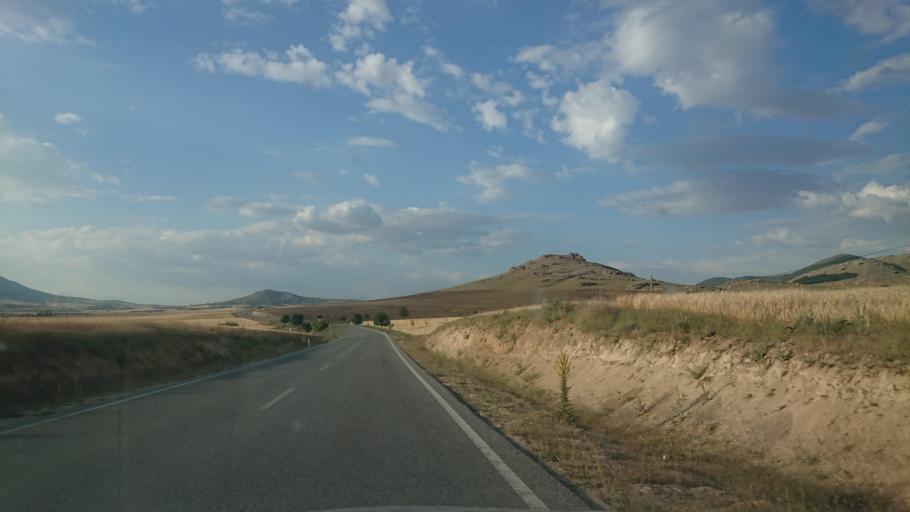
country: TR
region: Aksaray
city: Balci
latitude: 38.5454
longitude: 34.1027
